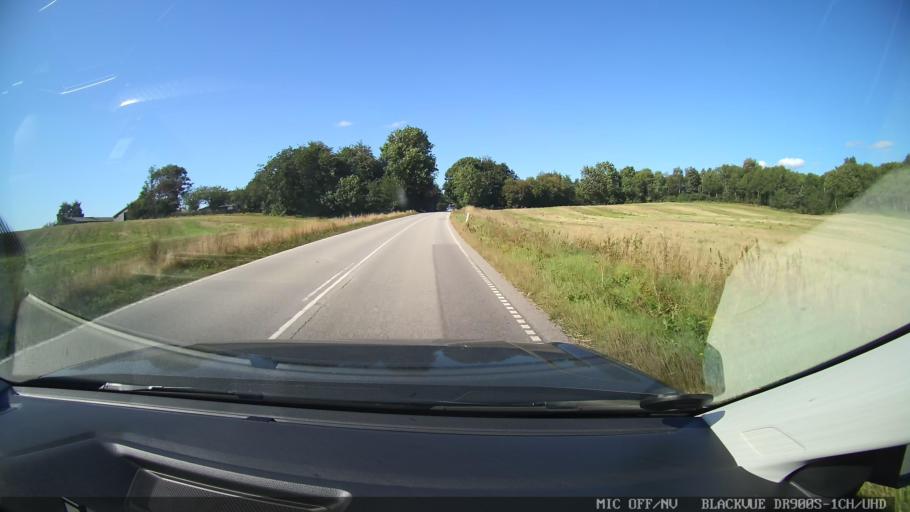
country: DK
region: North Denmark
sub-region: Mariagerfjord Kommune
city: Mariager
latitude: 56.6229
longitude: 9.9802
